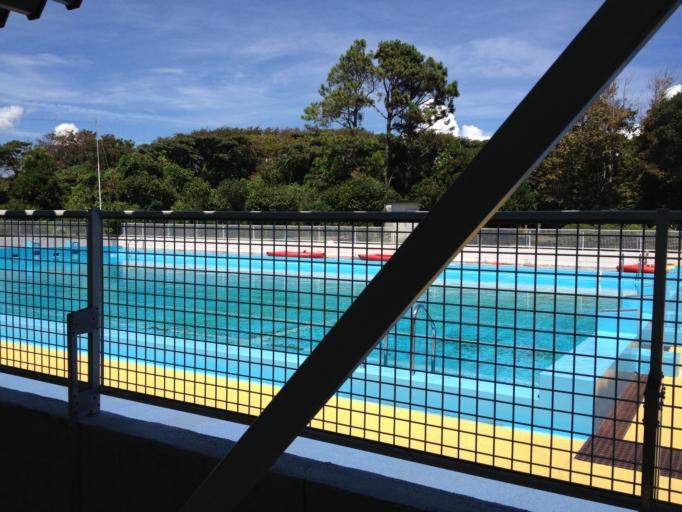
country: JP
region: Wakayama
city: Shingu
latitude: 33.4462
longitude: 135.7810
